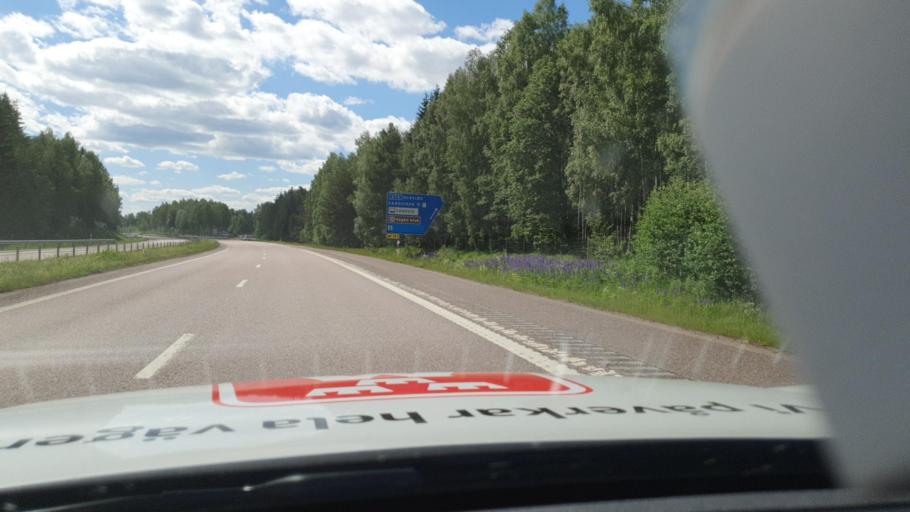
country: SE
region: Gaevleborg
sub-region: Sandvikens Kommun
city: Sandviken
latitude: 60.6341
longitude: 16.8118
